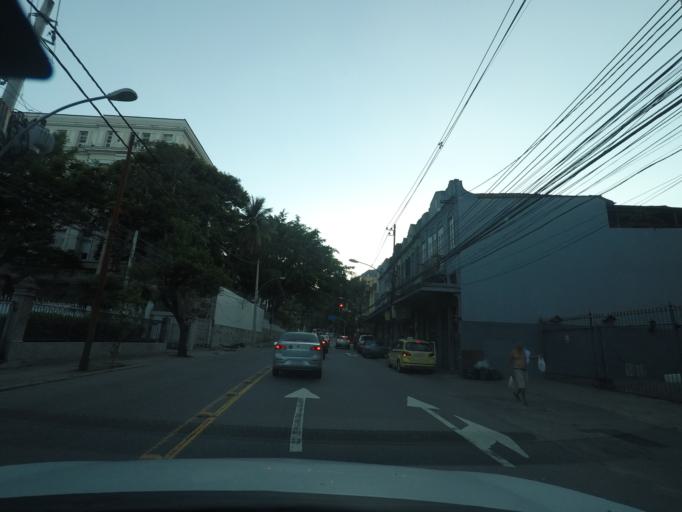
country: BR
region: Rio de Janeiro
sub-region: Rio De Janeiro
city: Rio de Janeiro
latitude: -22.9391
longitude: -43.2479
